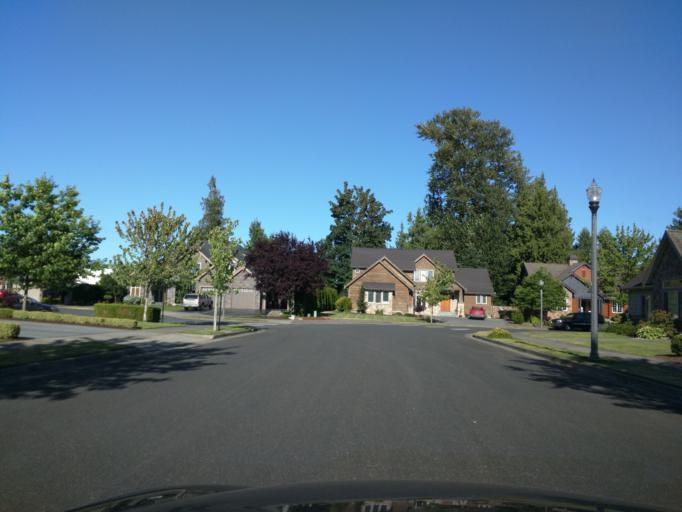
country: US
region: Washington
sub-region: Whatcom County
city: Lynden
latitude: 48.9550
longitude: -122.4592
